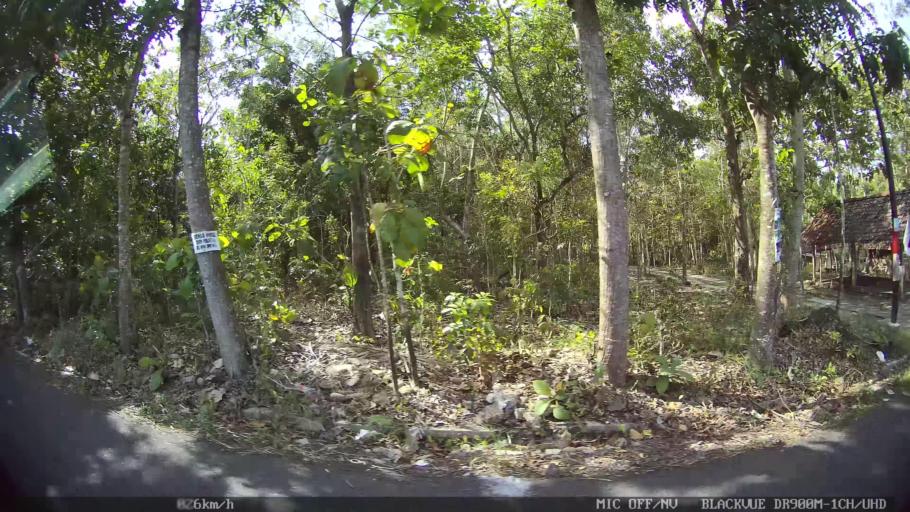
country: ID
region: Daerah Istimewa Yogyakarta
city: Bantul
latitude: -7.8594
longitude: 110.3029
